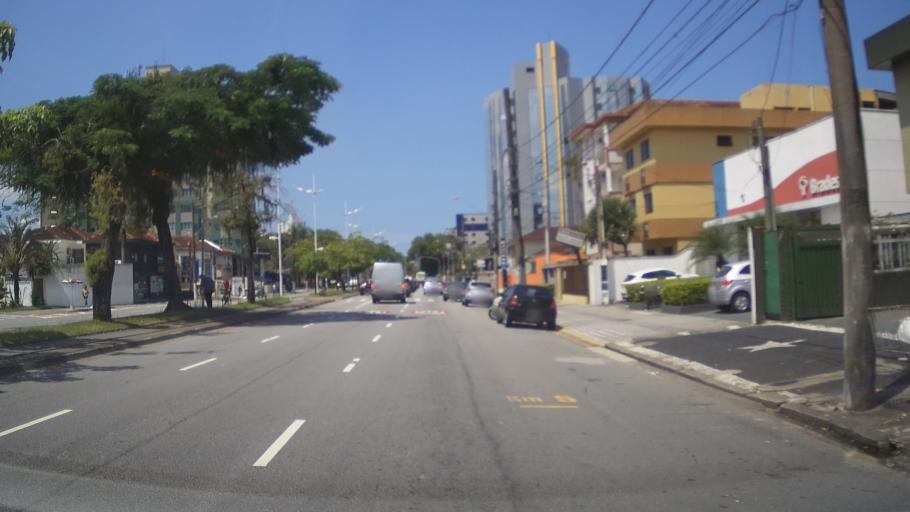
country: BR
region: Sao Paulo
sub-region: Santos
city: Santos
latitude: -23.9602
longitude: -46.3183
